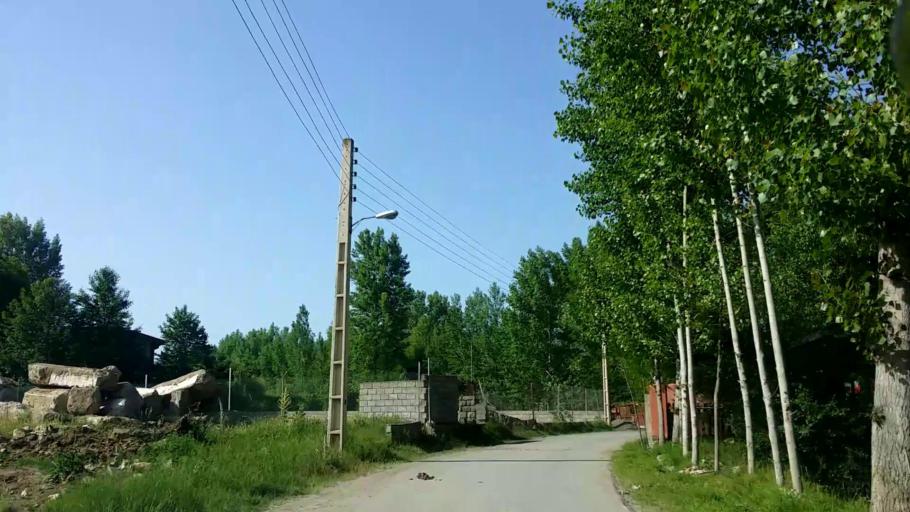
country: IR
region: Mazandaran
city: `Abbasabad
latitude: 36.5186
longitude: 51.1737
